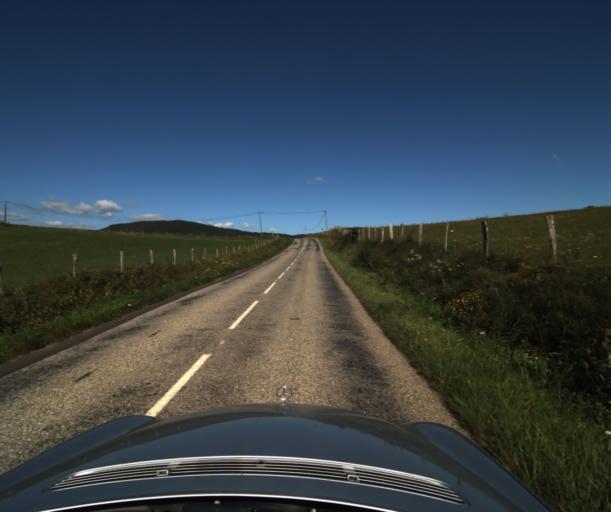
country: FR
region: Midi-Pyrenees
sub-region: Departement de l'Ariege
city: Lavelanet
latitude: 42.9923
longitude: 1.8898
